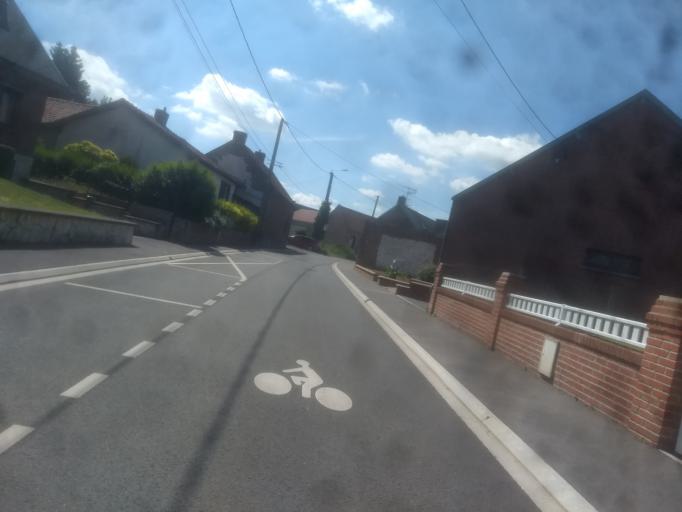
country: FR
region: Nord-Pas-de-Calais
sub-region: Departement du Pas-de-Calais
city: Agny
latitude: 50.2629
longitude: 2.7629
